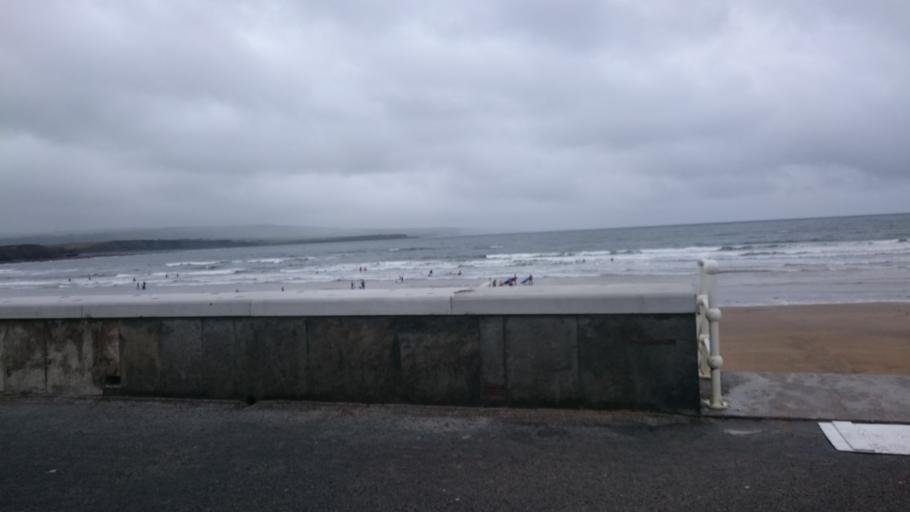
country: IE
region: Munster
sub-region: An Clar
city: Kilrush
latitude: 52.9354
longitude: -9.3506
